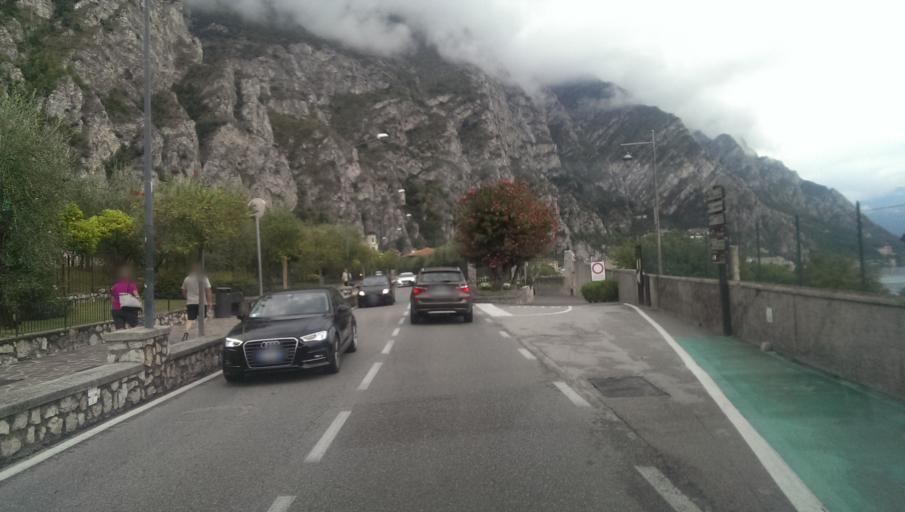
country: IT
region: Lombardy
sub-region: Provincia di Brescia
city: Limone sul Garda
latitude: 45.8114
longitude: 10.7921
